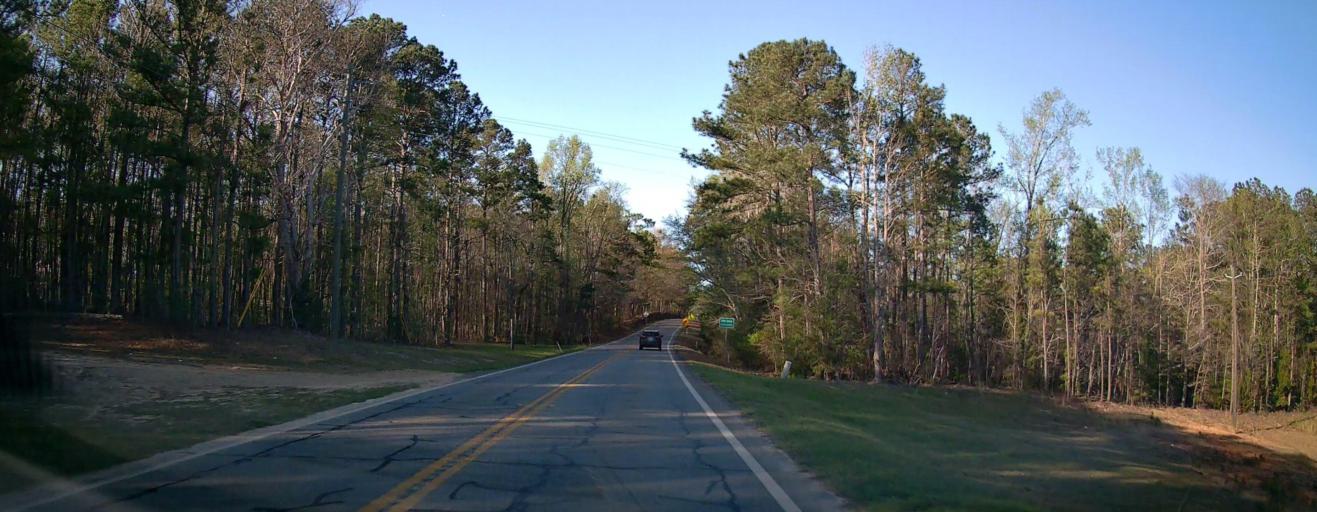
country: US
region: Georgia
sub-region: Butts County
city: Indian Springs
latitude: 33.2298
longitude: -83.9265
